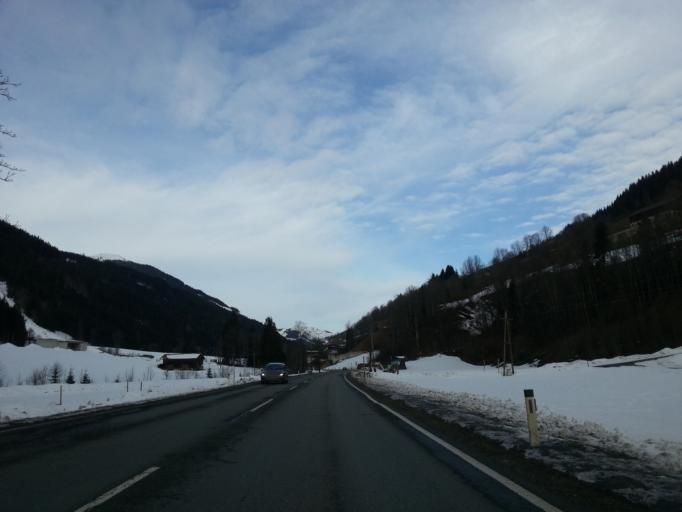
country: AT
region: Salzburg
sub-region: Politischer Bezirk Zell am See
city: Viehhofen
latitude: 47.3667
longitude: 12.7110
